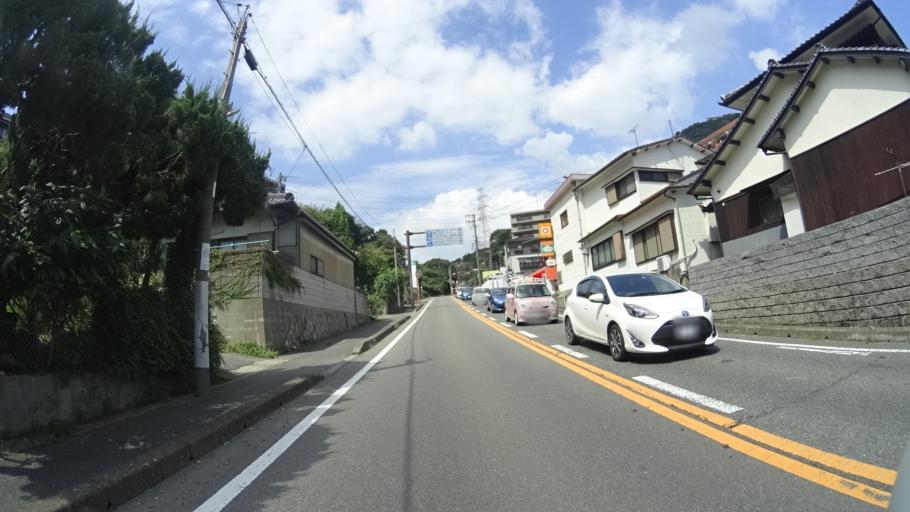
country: JP
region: Yamaguchi
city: Shimonoseki
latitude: 33.9674
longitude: 130.9550
